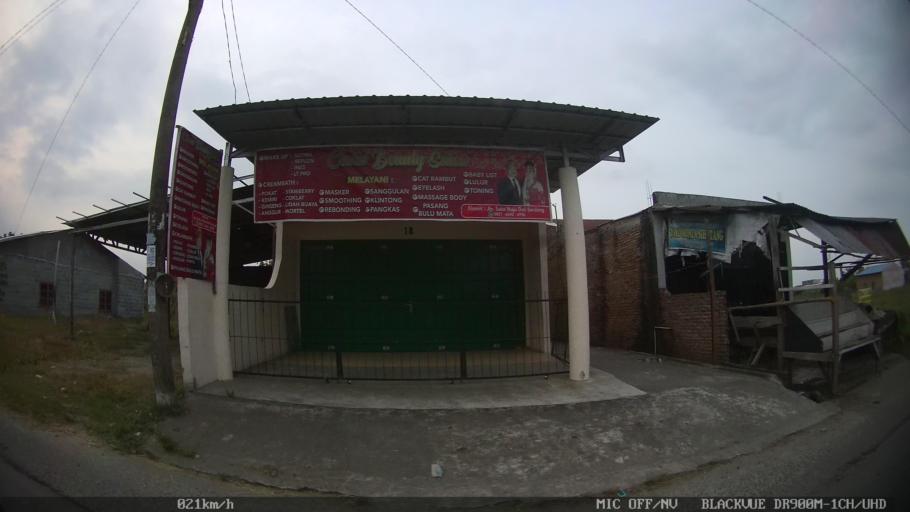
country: ID
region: North Sumatra
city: Sunggal
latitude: 3.5612
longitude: 98.5953
